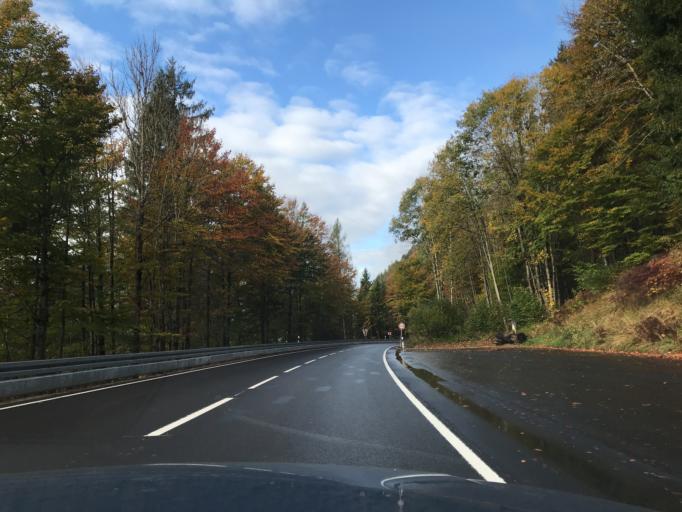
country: DE
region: Bavaria
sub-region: Upper Bavaria
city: Lenggries
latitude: 47.5786
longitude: 11.5419
